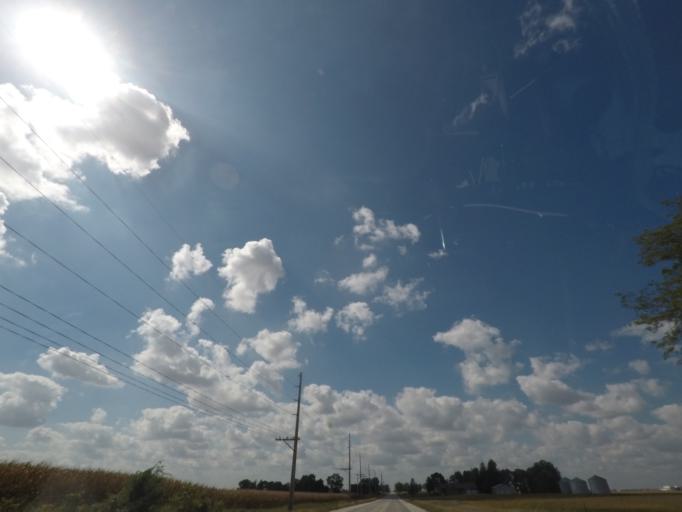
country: US
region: Iowa
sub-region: Story County
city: Nevada
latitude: 42.0231
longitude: -93.5346
